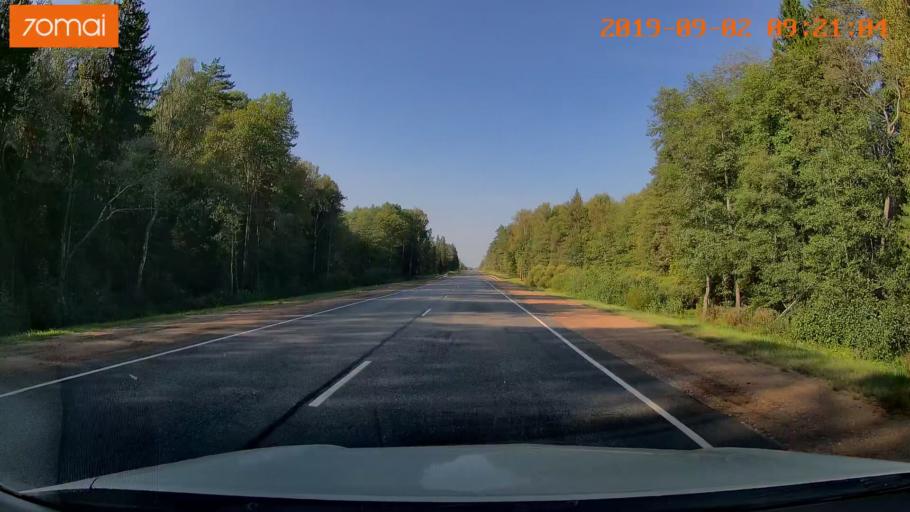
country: RU
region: Kaluga
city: Yukhnov
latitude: 54.7951
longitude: 35.3683
